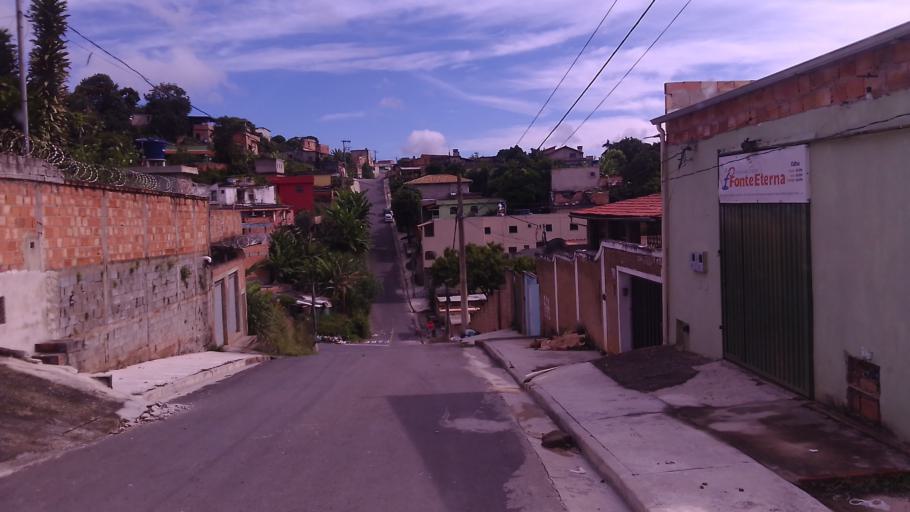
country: BR
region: Minas Gerais
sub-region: Santa Luzia
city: Santa Luzia
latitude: -19.8369
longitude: -43.8971
